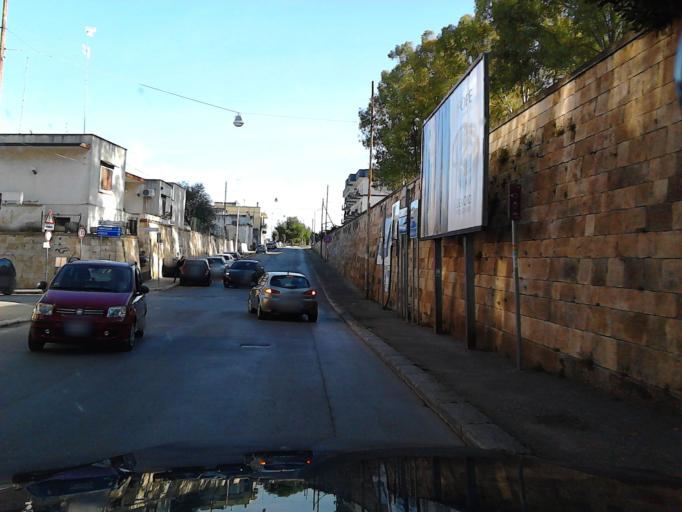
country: IT
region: Apulia
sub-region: Provincia di Bari
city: Mola di Bari
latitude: 41.0553
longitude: 17.0842
